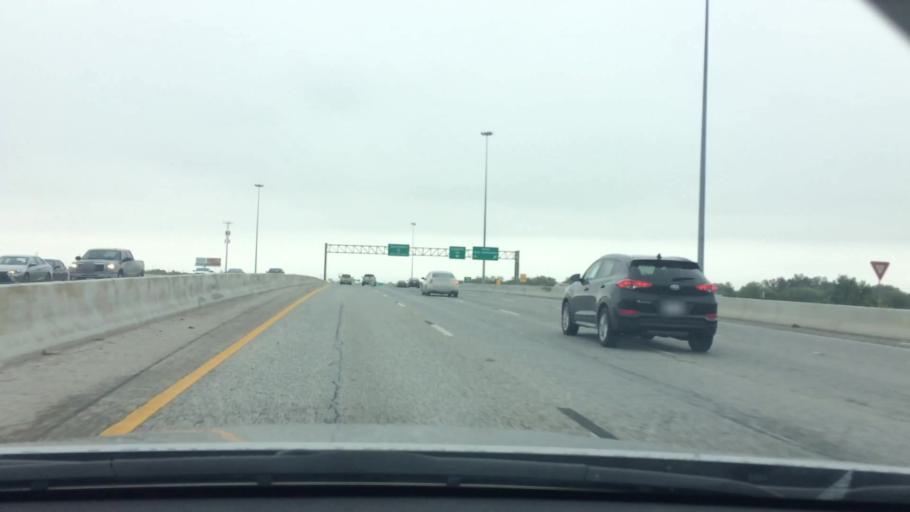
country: US
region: Texas
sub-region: Bexar County
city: Lackland Air Force Base
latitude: 29.4049
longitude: -98.5582
